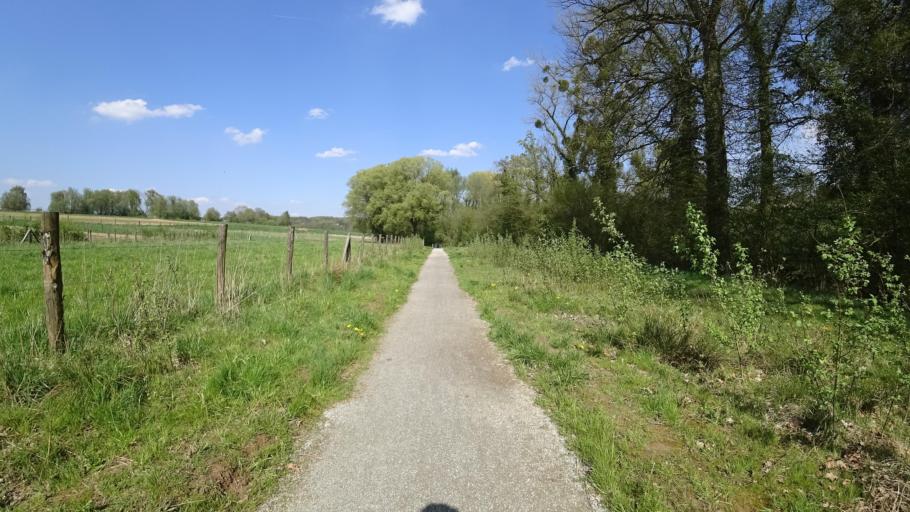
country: BE
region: Flanders
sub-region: Provincie Vlaams-Brabant
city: Beersel
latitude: 50.7269
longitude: 4.2877
